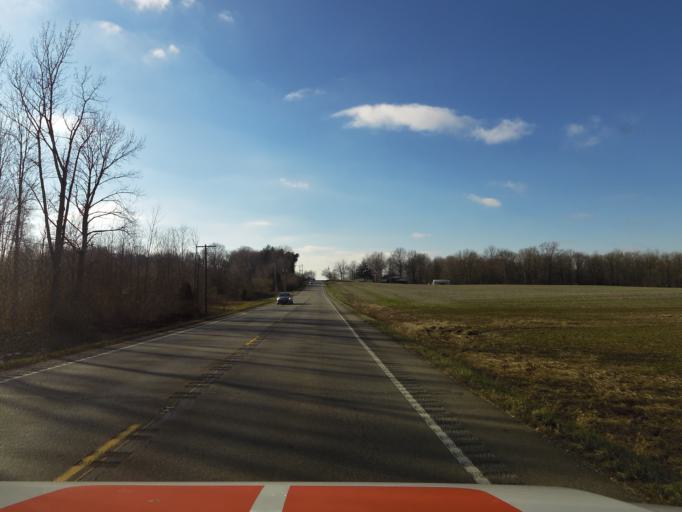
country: US
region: Indiana
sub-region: Jackson County
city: Seymour
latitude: 38.9639
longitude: -85.8209
